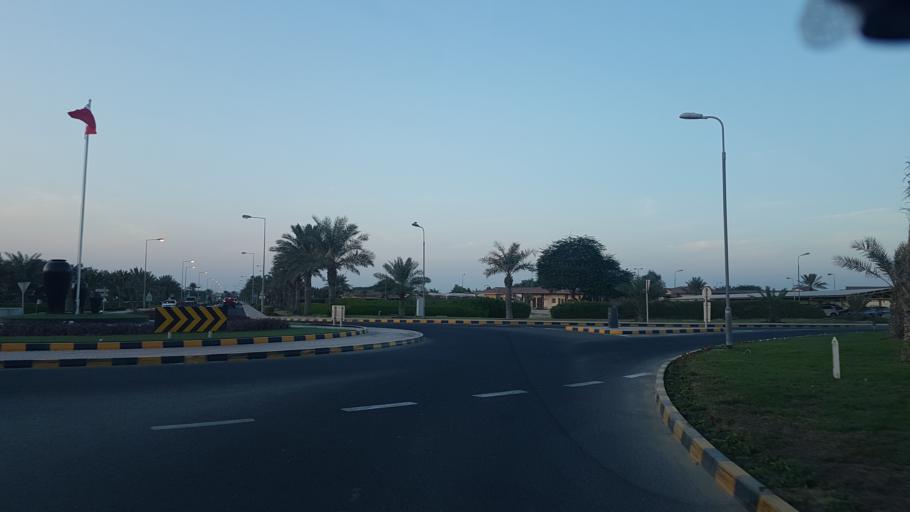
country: BH
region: Northern
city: Ar Rifa'
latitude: 26.0925
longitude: 50.5478
